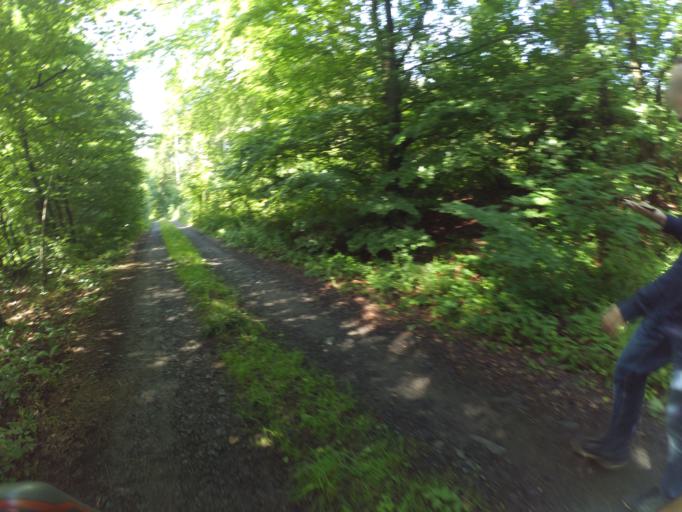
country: DE
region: Hesse
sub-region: Regierungsbezirk Kassel
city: Kirchheim
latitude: 50.8839
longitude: 9.5278
